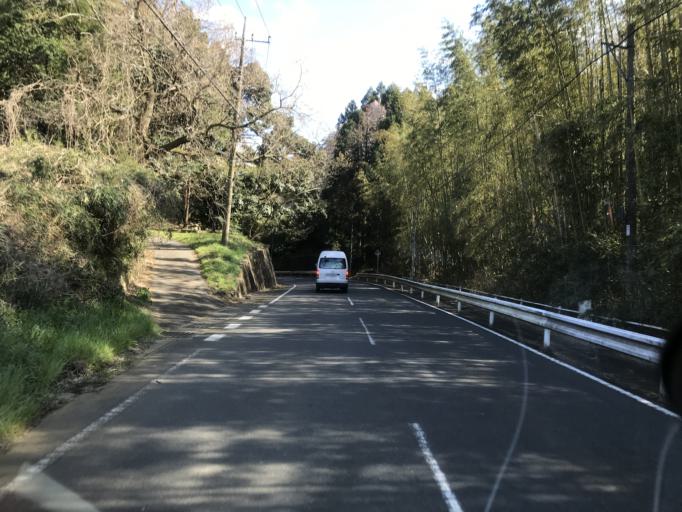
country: JP
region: Chiba
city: Sawara
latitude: 35.8522
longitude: 140.4190
